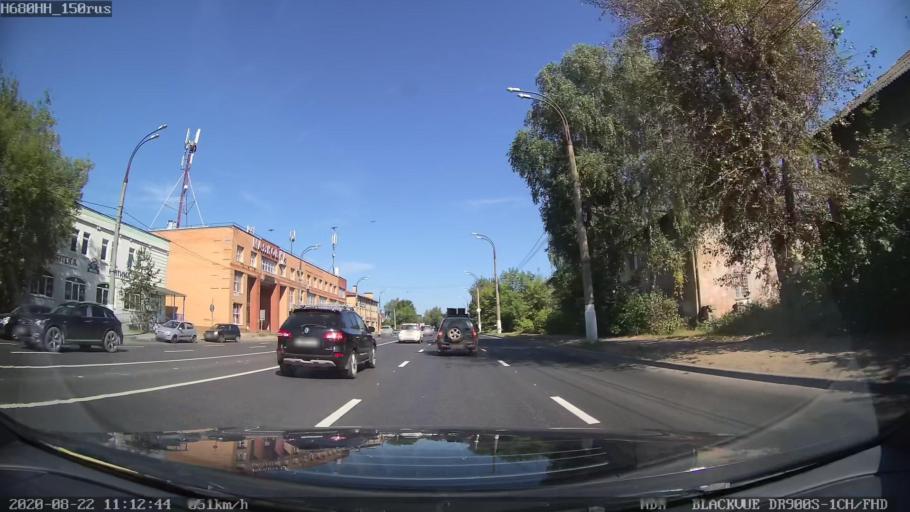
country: RU
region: Tverskaya
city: Tver
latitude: 56.8649
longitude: 35.9446
